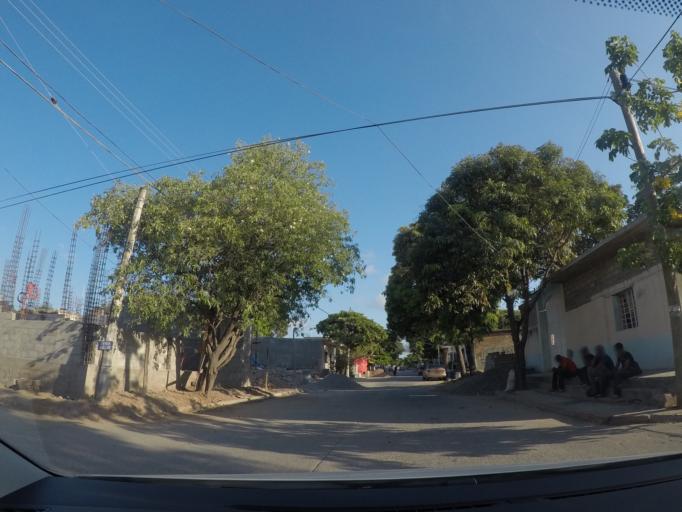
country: MX
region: Oaxaca
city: Juchitan de Zaragoza
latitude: 16.4347
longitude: -95.0291
